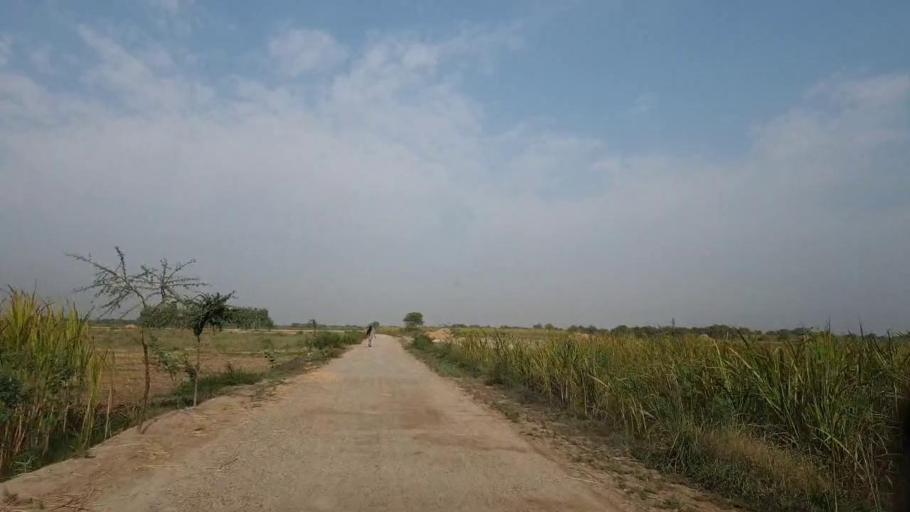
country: PK
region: Sindh
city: Tando Muhammad Khan
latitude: 25.0523
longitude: 68.4333
